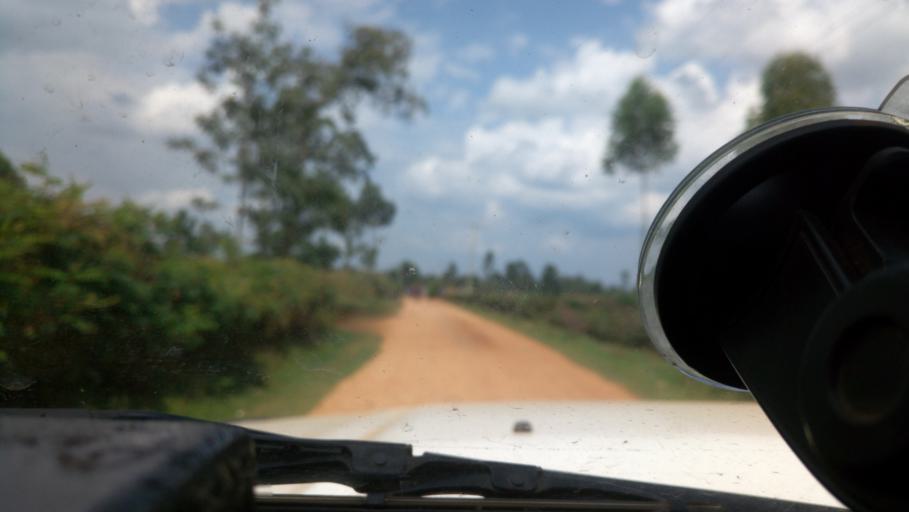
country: KE
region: Kericho
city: Sotik
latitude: -0.6541
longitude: 35.0928
